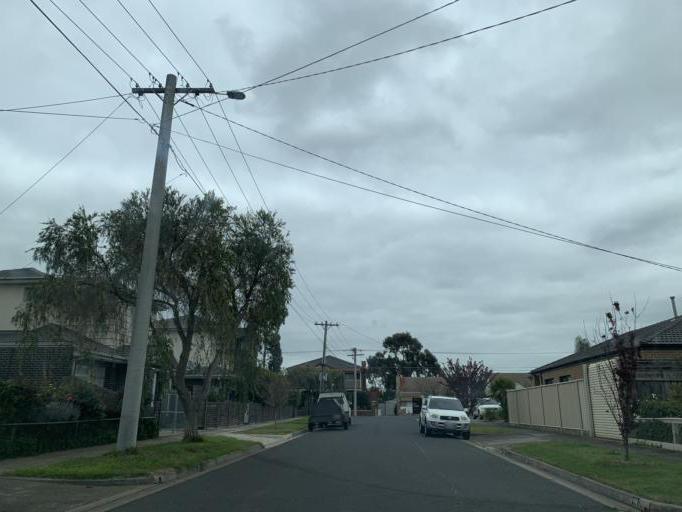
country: AU
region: Victoria
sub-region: Moreland
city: Pascoe Vale
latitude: -37.7255
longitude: 144.9439
